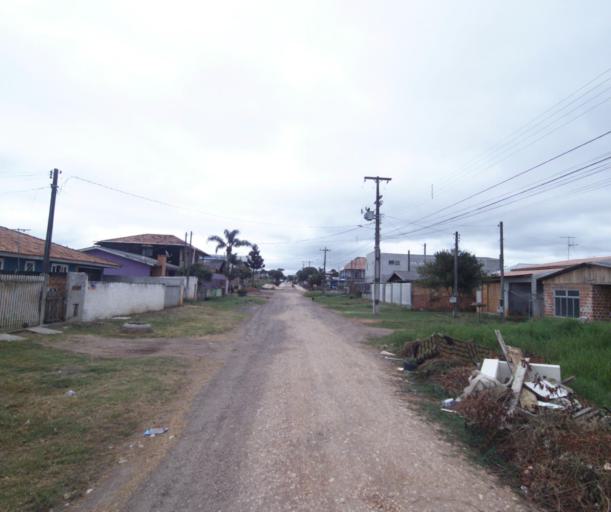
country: BR
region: Parana
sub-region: Quatro Barras
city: Quatro Barras
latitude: -25.3643
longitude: -49.0919
